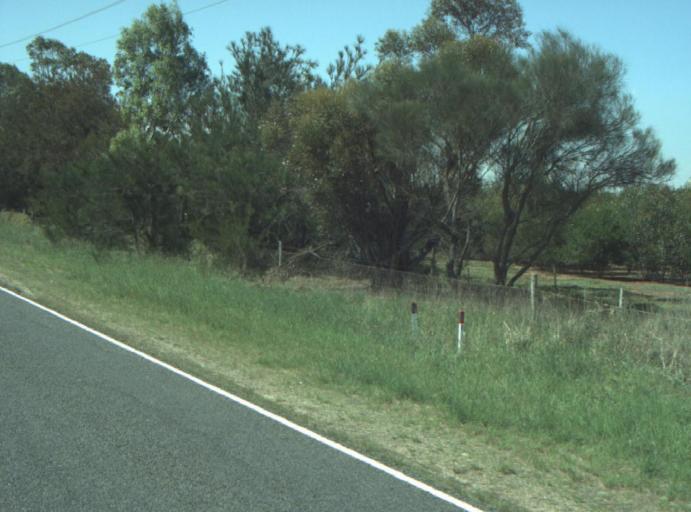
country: AU
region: Victoria
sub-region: Greater Geelong
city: Lara
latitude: -38.0033
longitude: 144.3998
